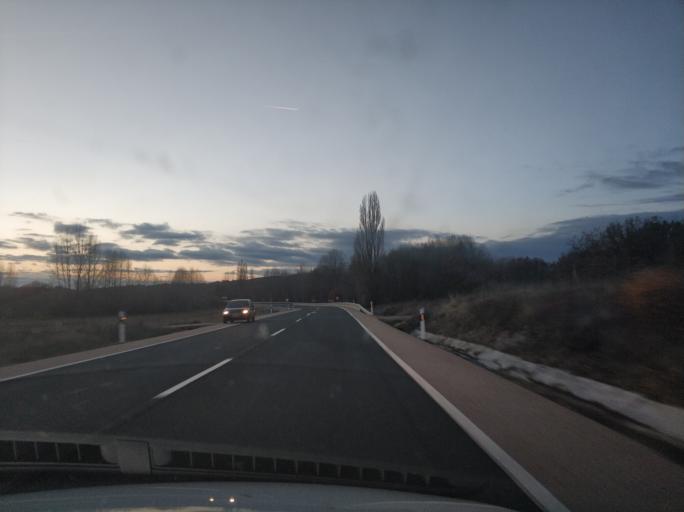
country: ES
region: Castille and Leon
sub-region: Provincia de Soria
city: Cidones
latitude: 41.8130
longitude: -2.7077
